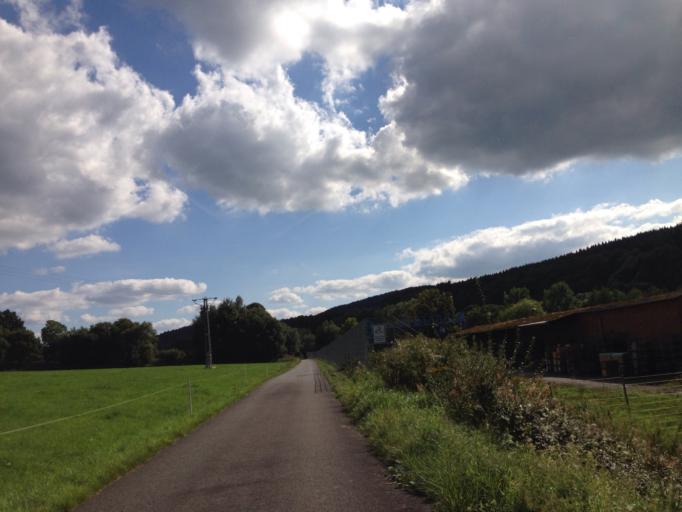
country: DE
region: Hesse
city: Hatzfeld
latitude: 51.0025
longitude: 8.5856
